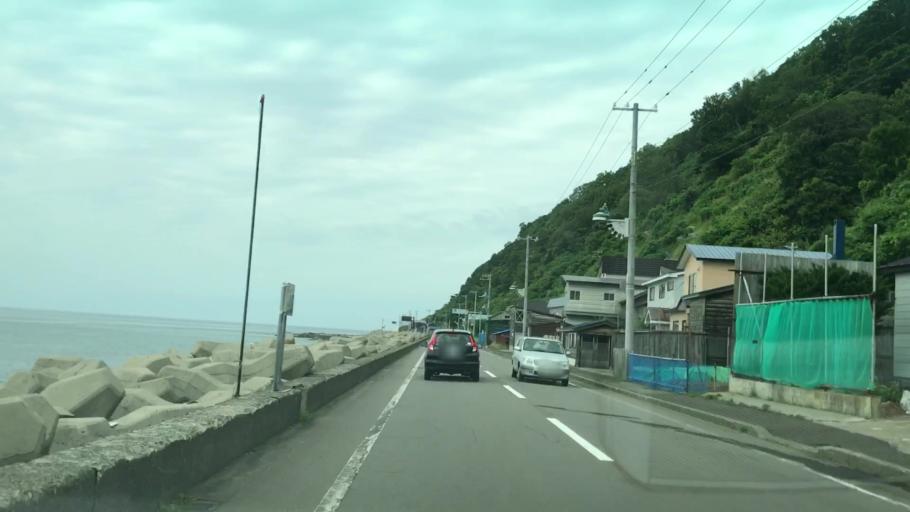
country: JP
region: Hokkaido
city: Iwanai
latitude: 43.1605
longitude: 140.3970
